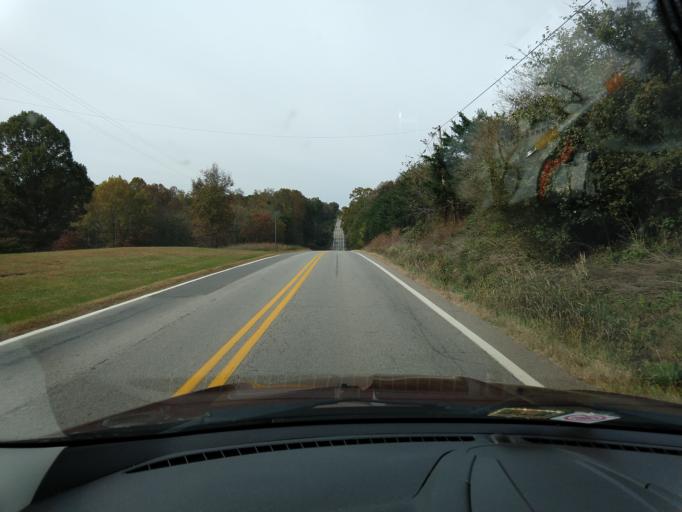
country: US
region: Virginia
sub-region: Pittsylvania County
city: Gretna
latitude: 36.9449
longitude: -79.4862
